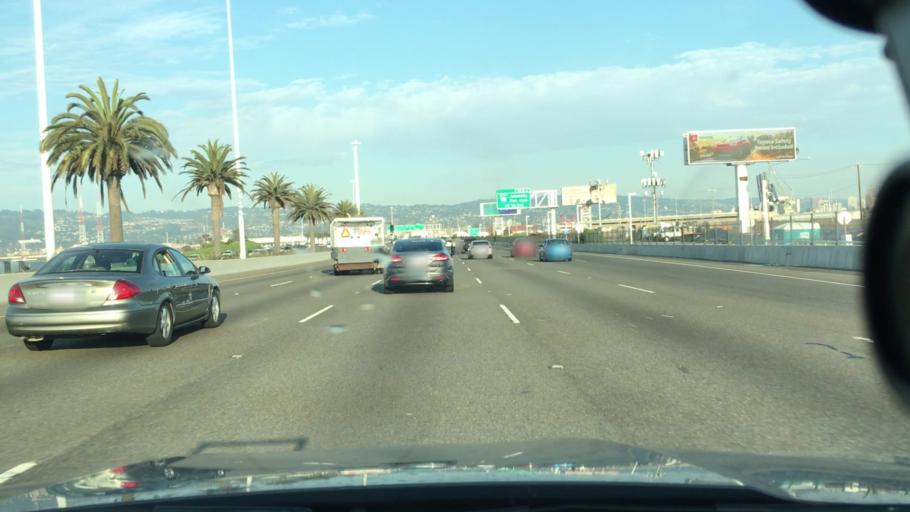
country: US
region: California
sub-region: Alameda County
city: Emeryville
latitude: 37.8215
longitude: -122.3261
